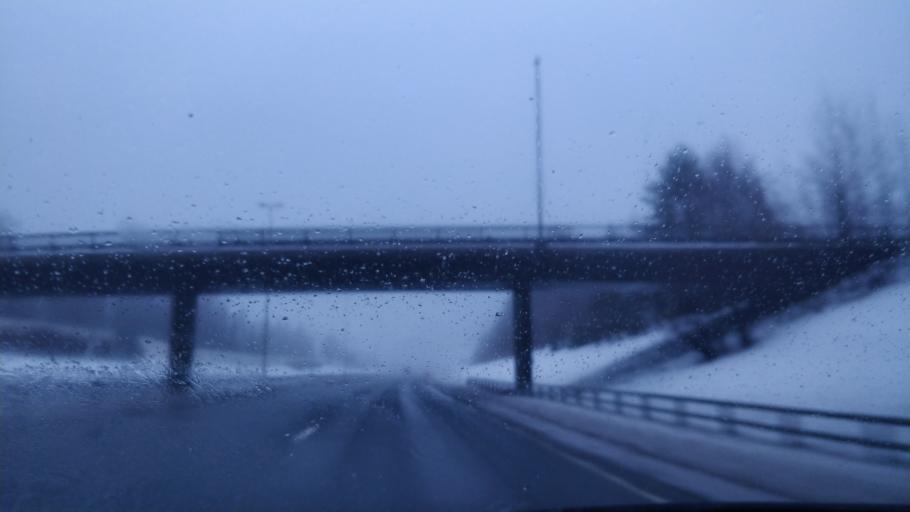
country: FI
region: Lapland
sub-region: Kemi-Tornio
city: Kemi
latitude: 65.7504
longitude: 24.5757
